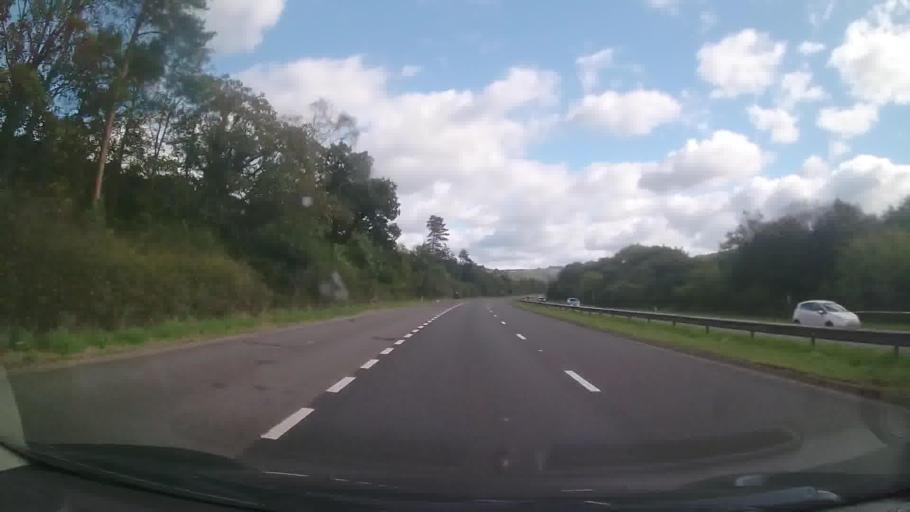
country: GB
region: Wales
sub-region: Neath Port Talbot
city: Glyn-neath
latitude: 51.7515
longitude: -3.6056
